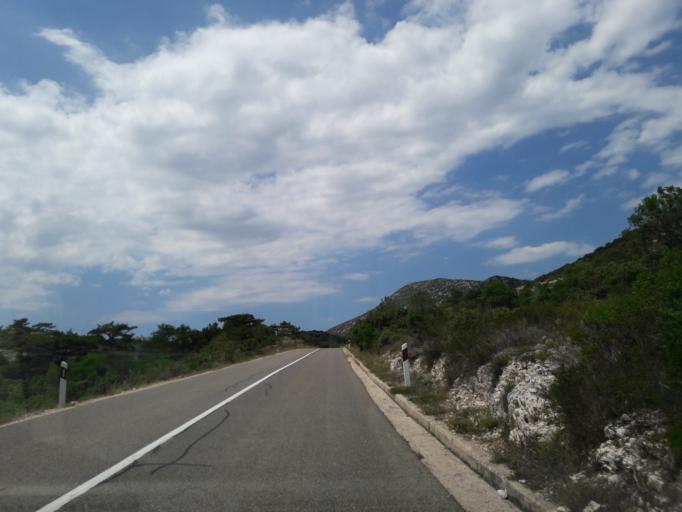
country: HR
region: Dubrovacko-Neretvanska
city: Orebic
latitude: 42.9729
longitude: 17.2751
